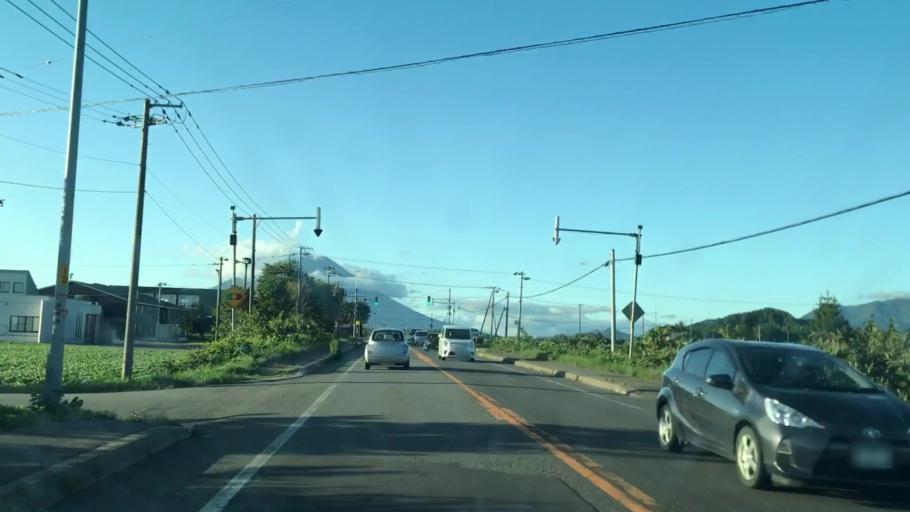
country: JP
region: Hokkaido
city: Niseko Town
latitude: 42.6733
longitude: 140.8421
